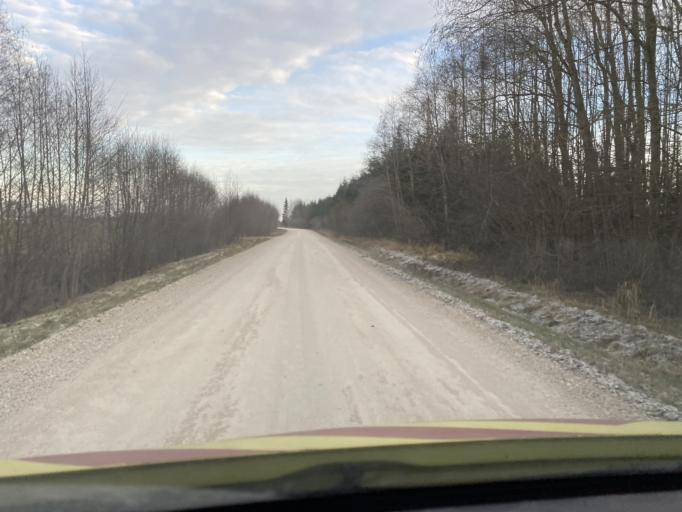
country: EE
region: Jogevamaa
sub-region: Poltsamaa linn
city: Poltsamaa
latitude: 58.5825
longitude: 26.1711
